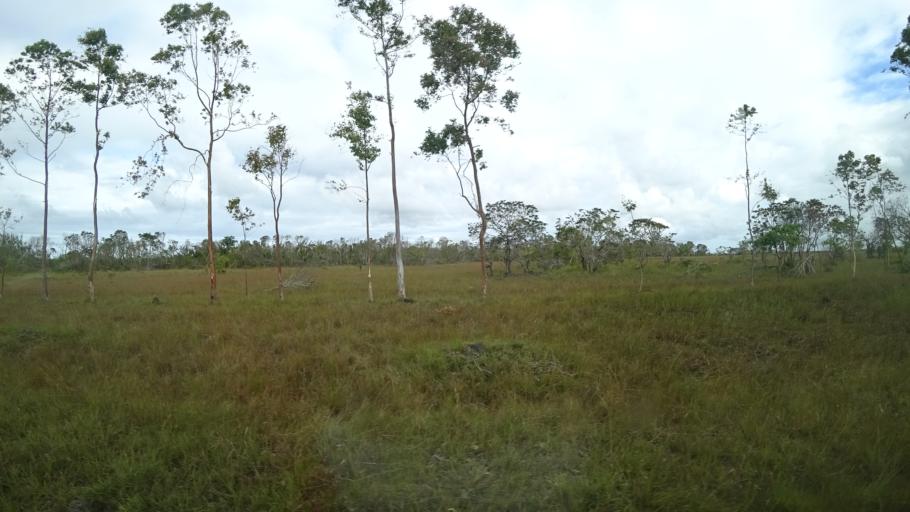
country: MZ
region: Sofala
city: Beira
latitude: -19.6110
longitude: 35.0809
